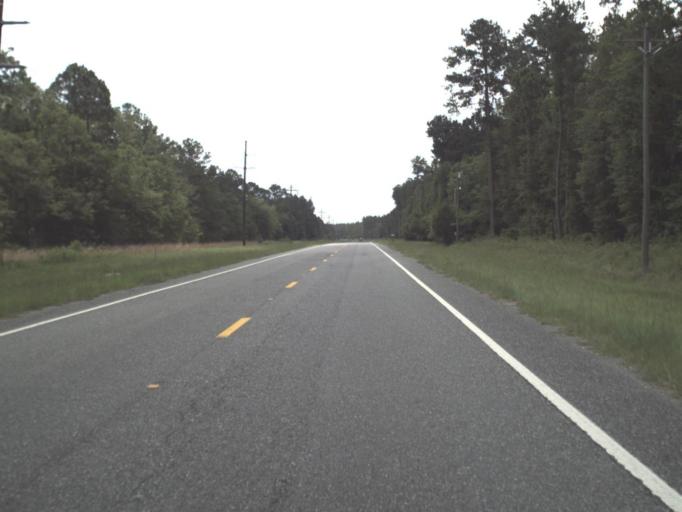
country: US
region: Florida
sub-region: Union County
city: Lake Butler
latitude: 29.9906
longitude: -82.2608
